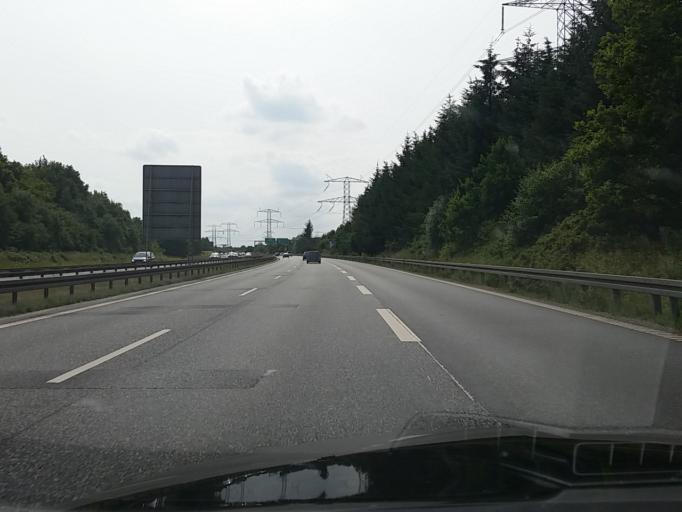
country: DK
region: South Denmark
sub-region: Kolding Kommune
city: Kolding
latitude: 55.5252
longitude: 9.4498
